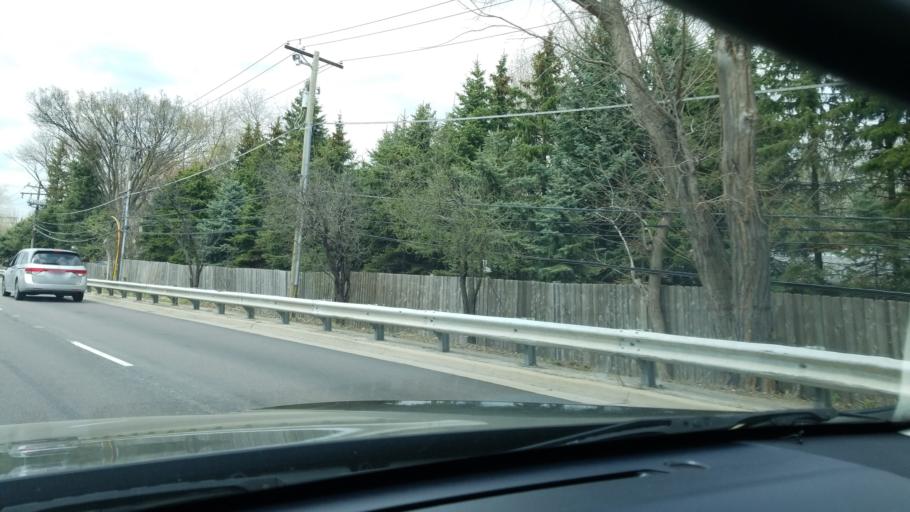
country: US
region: Illinois
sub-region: Cook County
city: Rolling Meadows
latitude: 42.0657
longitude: -88.0372
